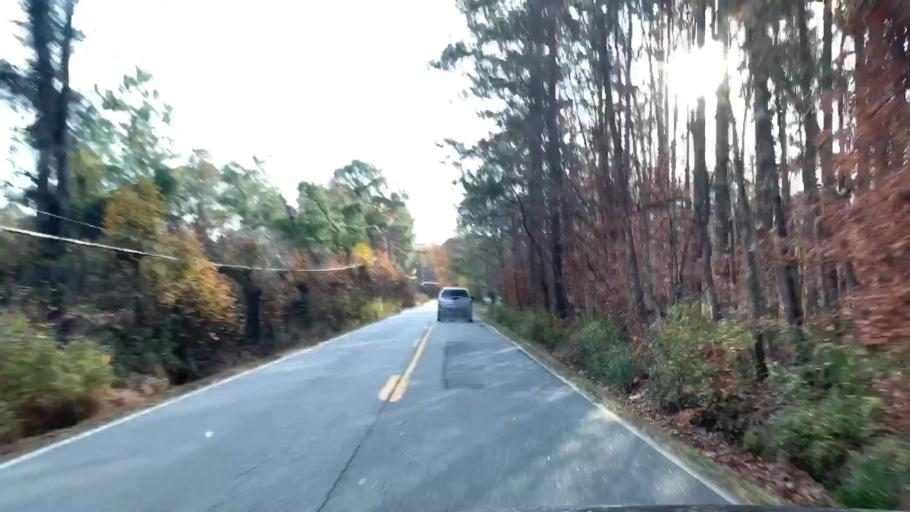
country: US
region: Virginia
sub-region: City of Virginia Beach
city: Virginia Beach
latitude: 36.7375
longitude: -76.1036
